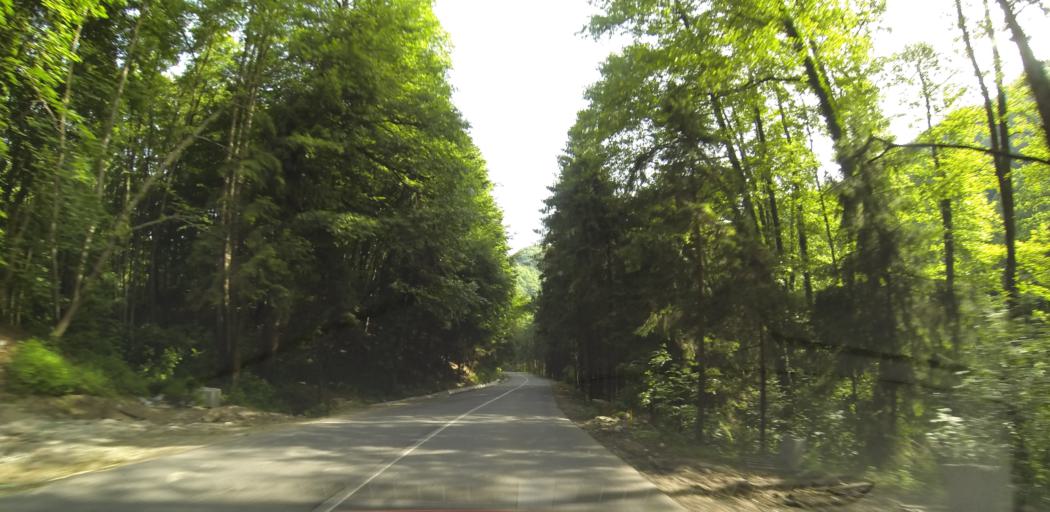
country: RO
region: Valcea
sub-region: Oras Baile Olanesti
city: Livadia
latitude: 45.1964
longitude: 24.2504
